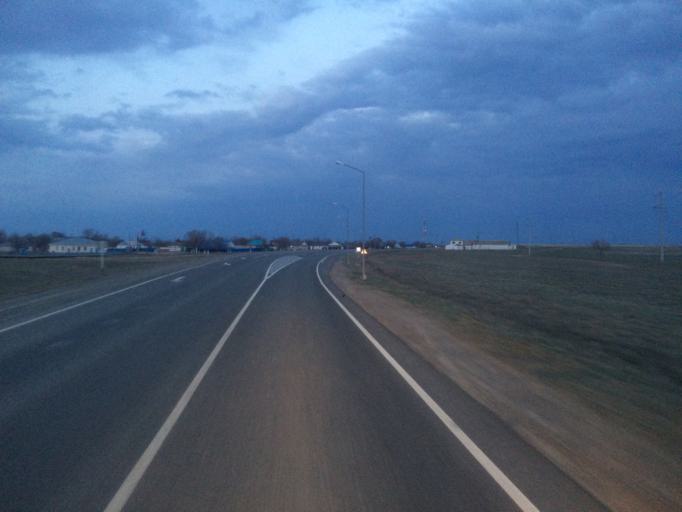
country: KZ
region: Aqtoebe
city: Martuk
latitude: 50.6400
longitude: 56.6871
